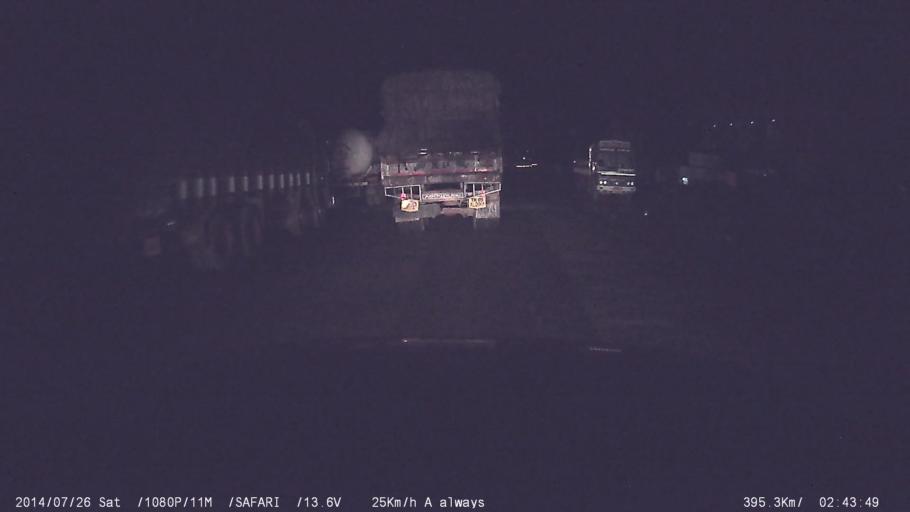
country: IN
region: Kerala
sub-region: Palakkad district
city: Palakkad
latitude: 10.7722
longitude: 76.6872
